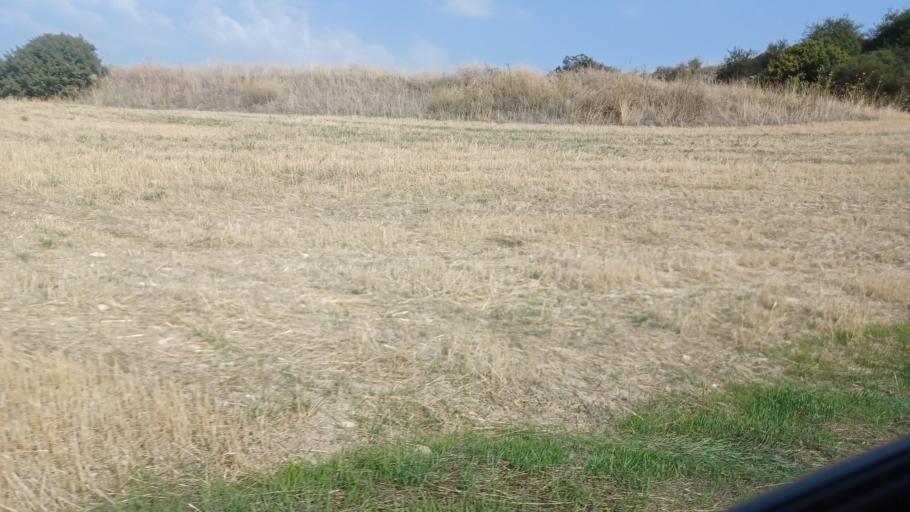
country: CY
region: Pafos
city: Polis
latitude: 34.9896
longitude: 32.4587
